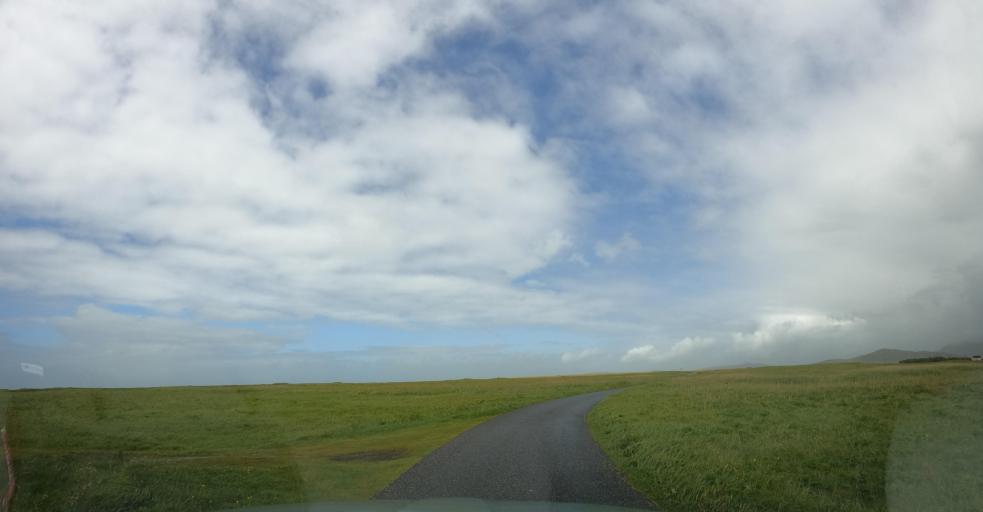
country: GB
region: Scotland
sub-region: Eilean Siar
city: Isle of South Uist
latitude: 57.2845
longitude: -7.4192
